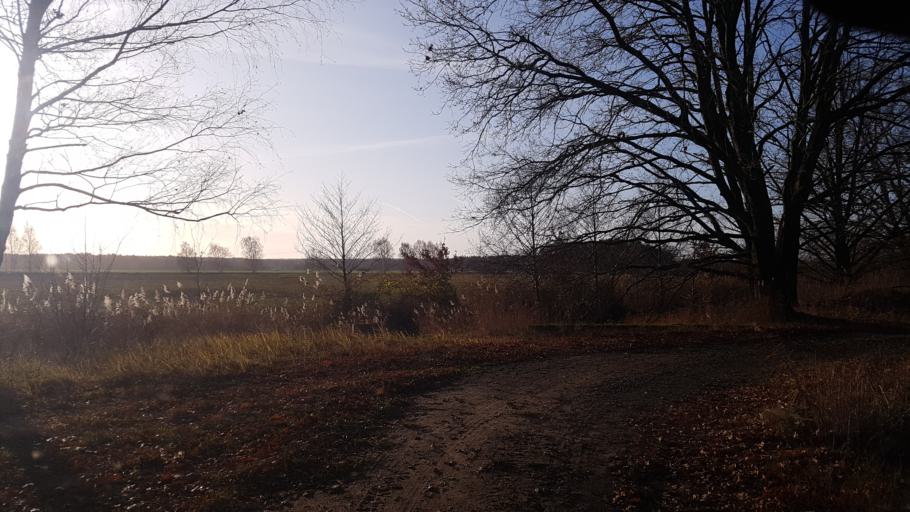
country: DE
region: Brandenburg
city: Schonborn
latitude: 51.5710
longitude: 13.4953
